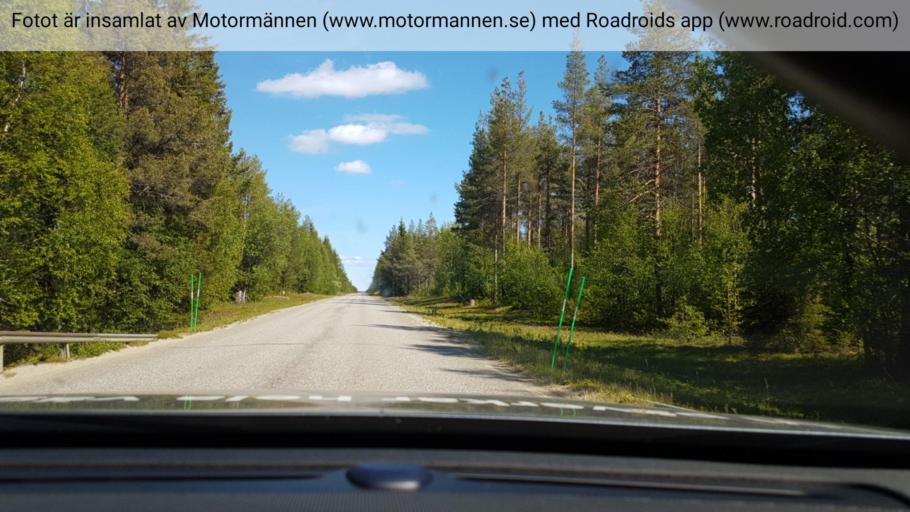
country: SE
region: Vaesterbotten
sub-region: Lycksele Kommun
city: Soderfors
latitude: 64.6338
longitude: 17.9311
